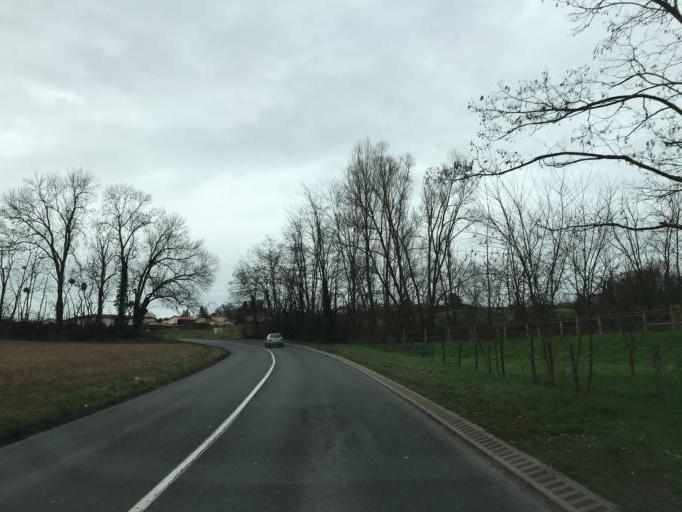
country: FR
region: Rhone-Alpes
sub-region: Departement de l'Ain
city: Jassans-Riottier
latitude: 45.9849
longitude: 4.7673
